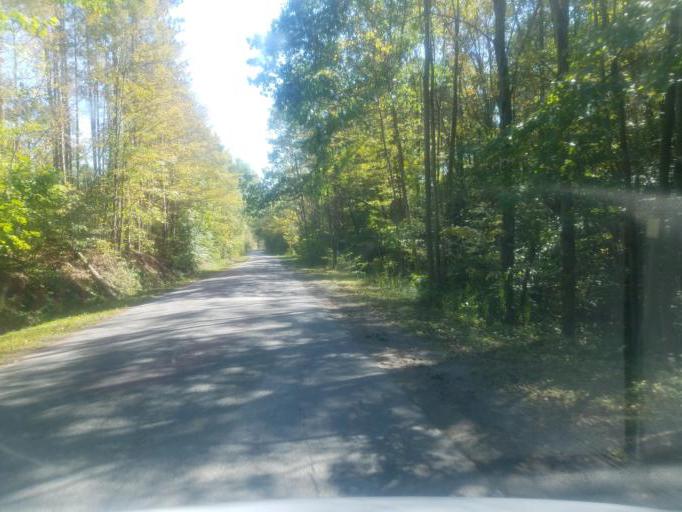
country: US
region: New York
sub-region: Allegany County
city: Cuba
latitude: 42.3077
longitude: -78.2022
